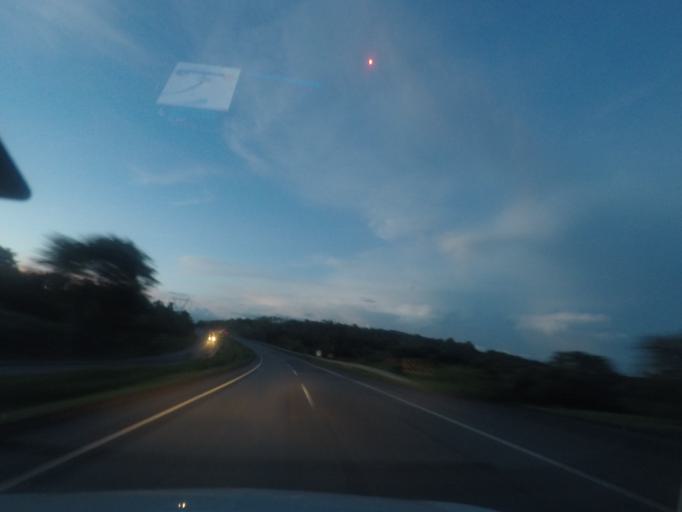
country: BR
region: Goias
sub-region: Piracanjuba
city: Piracanjuba
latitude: -17.3991
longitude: -49.2231
